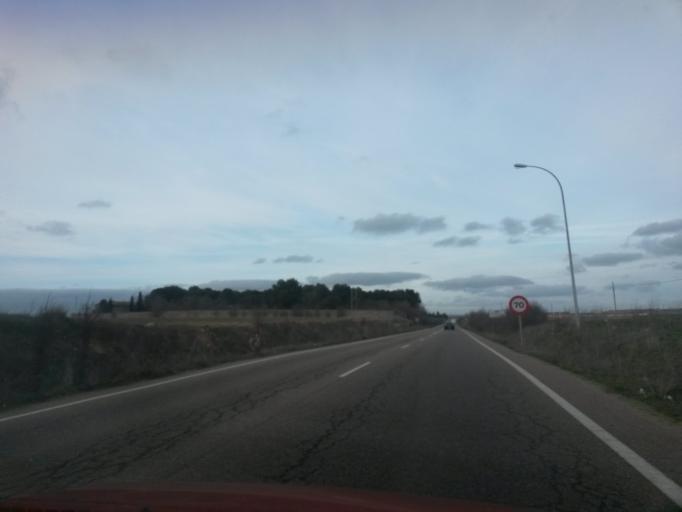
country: ES
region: Castille and Leon
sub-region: Provincia de Salamanca
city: Salamanca
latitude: 40.9847
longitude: -5.6600
